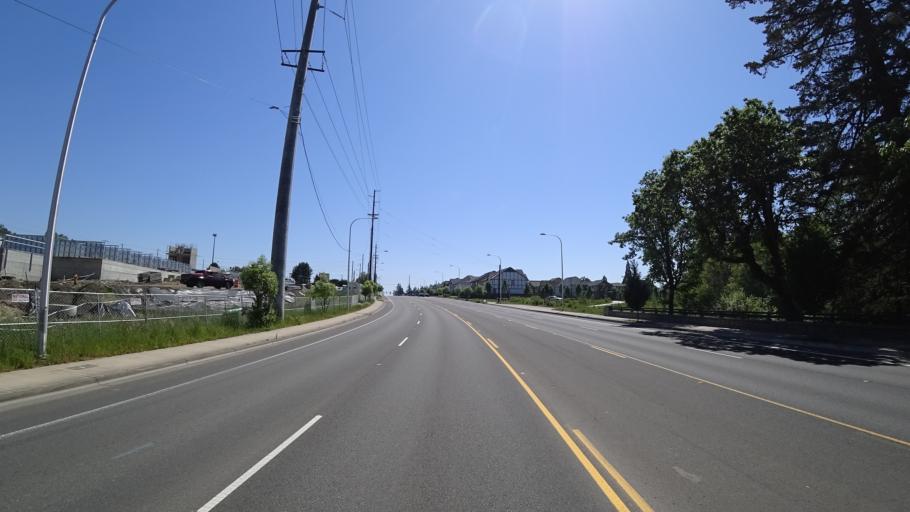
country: US
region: Oregon
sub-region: Washington County
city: Rockcreek
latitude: 45.5264
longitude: -122.8999
